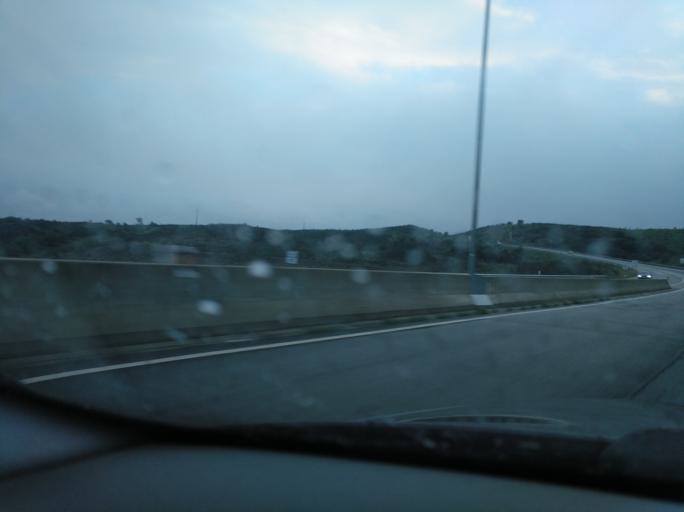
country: PT
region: Faro
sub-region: Castro Marim
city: Castro Marim
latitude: 37.3133
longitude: -7.4896
